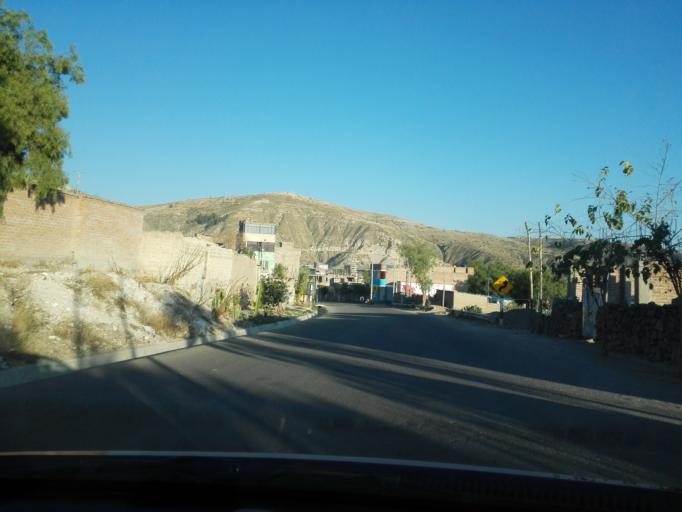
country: PE
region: Ayacucho
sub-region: Provincia de Huamanga
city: Ayacucho
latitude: -13.1365
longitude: -74.2234
